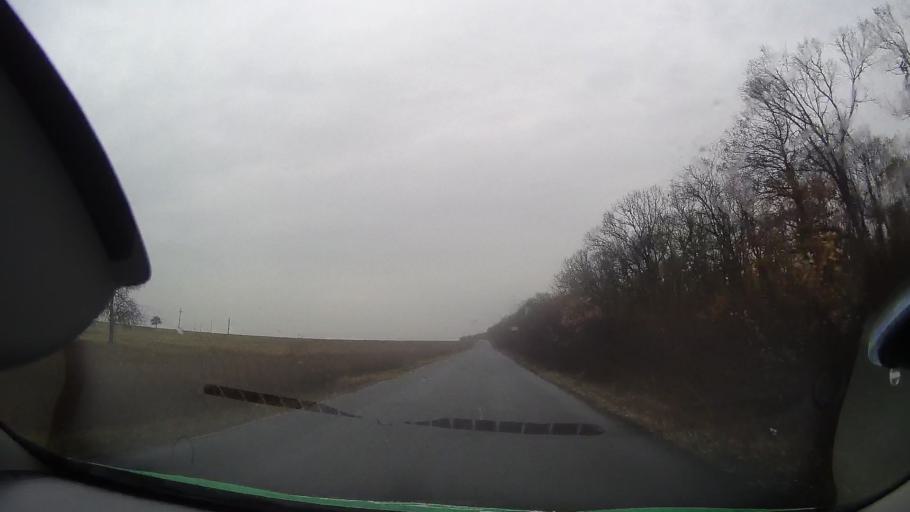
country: RO
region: Bihor
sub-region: Comuna Tinca
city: Gurbediu
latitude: 46.7757
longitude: 21.8808
